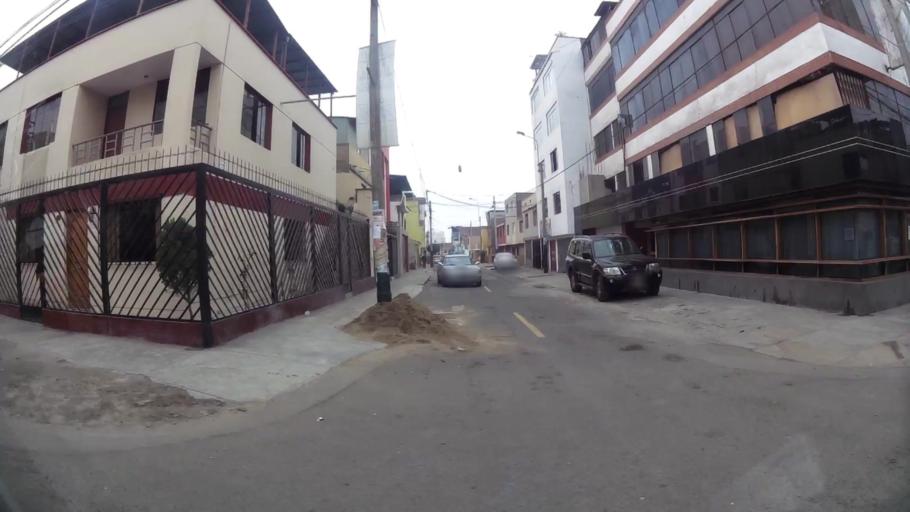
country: PE
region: Lima
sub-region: Lima
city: Surco
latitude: -12.1584
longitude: -76.9744
